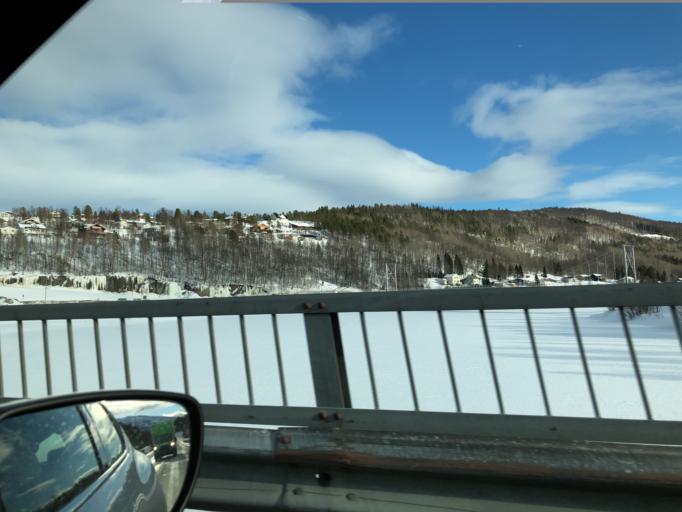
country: NO
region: Troms
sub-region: Malselv
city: Moen
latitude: 69.1394
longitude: 18.5960
